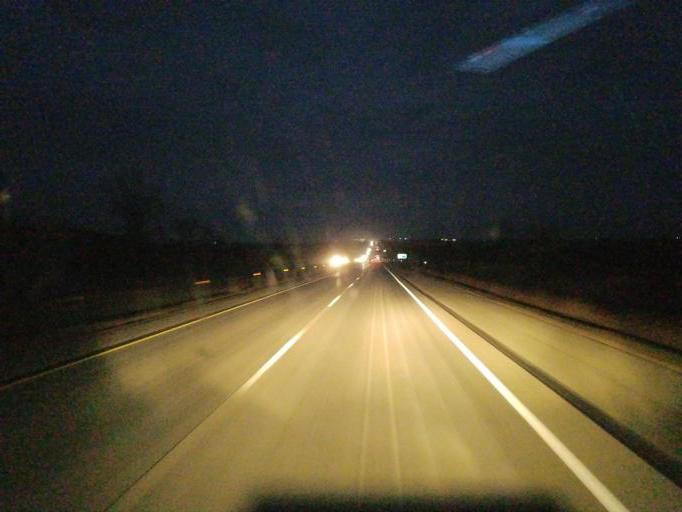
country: US
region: Iowa
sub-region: Guthrie County
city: Stuart
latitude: 41.4960
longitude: -94.4914
